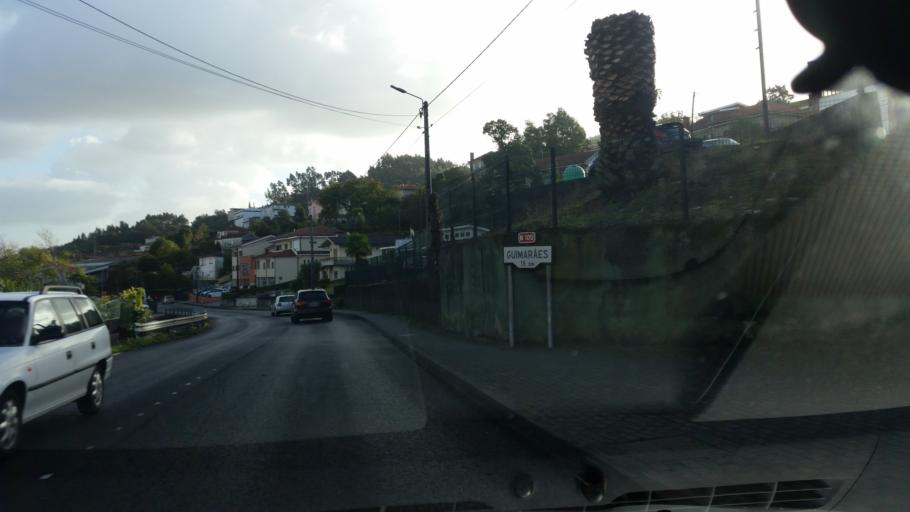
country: PT
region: Porto
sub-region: Santo Tirso
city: Negrelos
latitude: 41.3554
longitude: -8.4055
